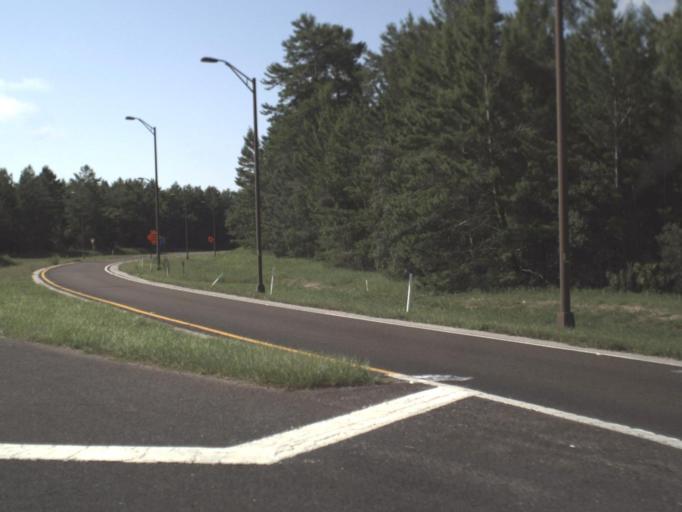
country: US
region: Florida
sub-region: Citrus County
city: Sugarmill Woods
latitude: 28.6868
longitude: -82.4975
